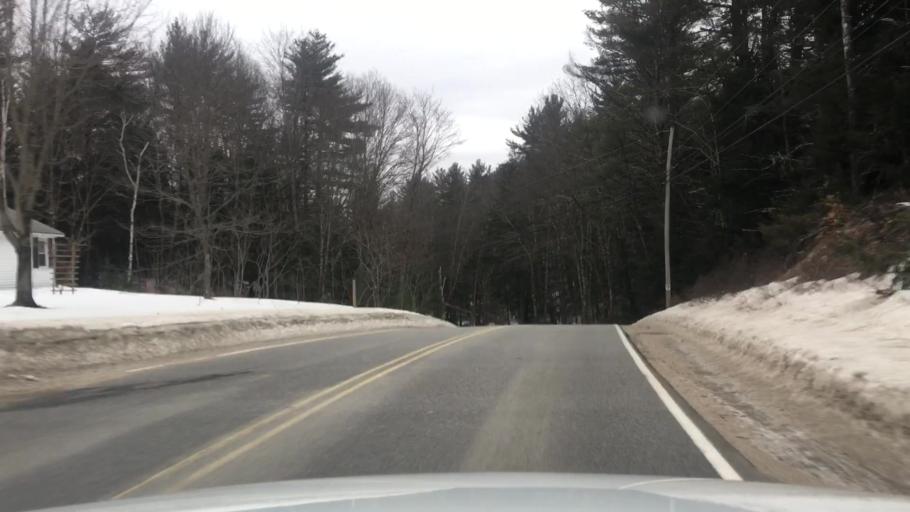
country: US
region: Maine
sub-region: York County
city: Springvale
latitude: 43.5060
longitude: -70.8151
